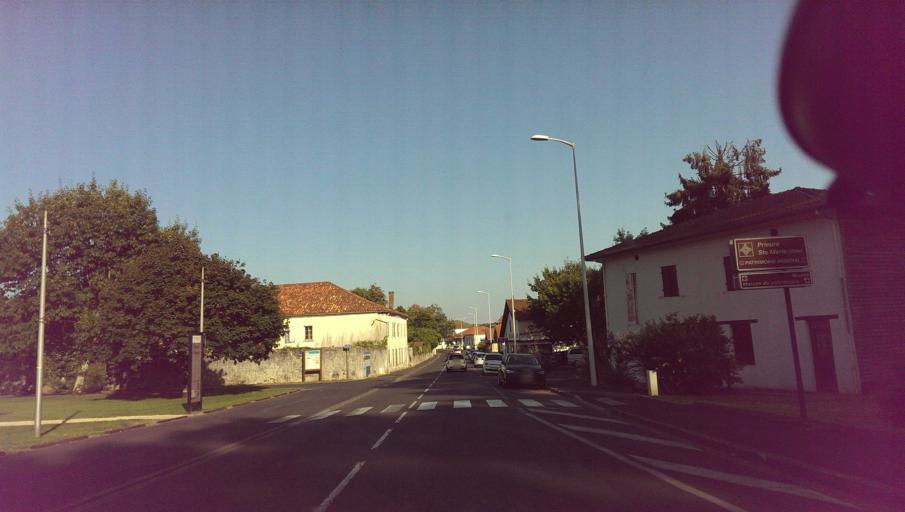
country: FR
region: Aquitaine
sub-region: Departement des Landes
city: Mimizan
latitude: 44.2037
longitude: -1.2361
